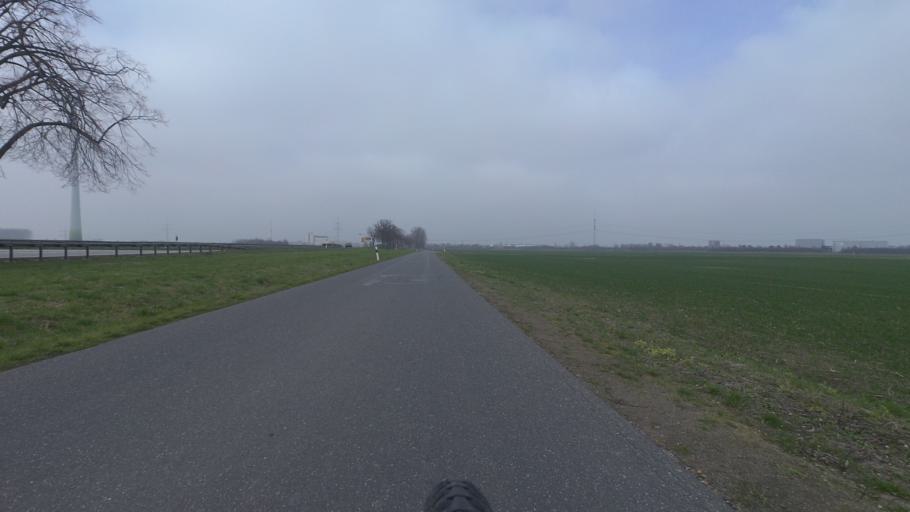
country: DE
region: Brandenburg
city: Nauen
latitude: 52.5888
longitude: 12.8956
